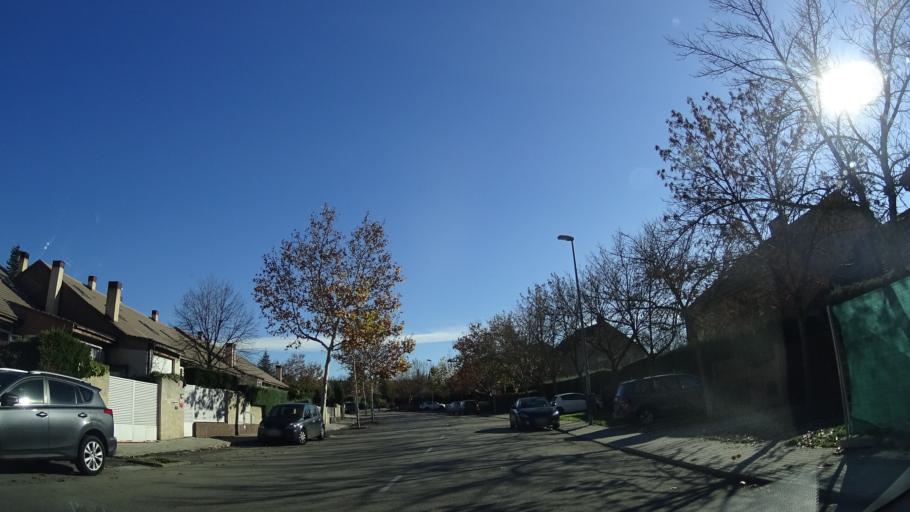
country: ES
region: Madrid
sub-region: Provincia de Madrid
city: Las Matas
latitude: 40.5211
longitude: -3.9106
